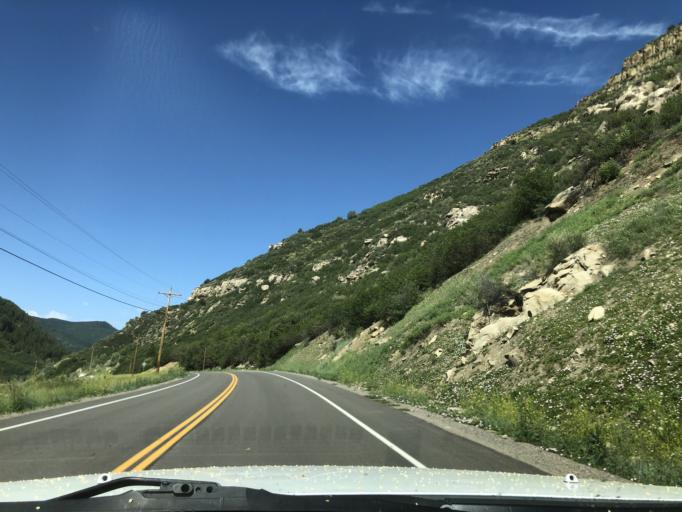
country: US
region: Colorado
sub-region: Delta County
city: Paonia
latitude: 38.9340
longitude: -107.4003
